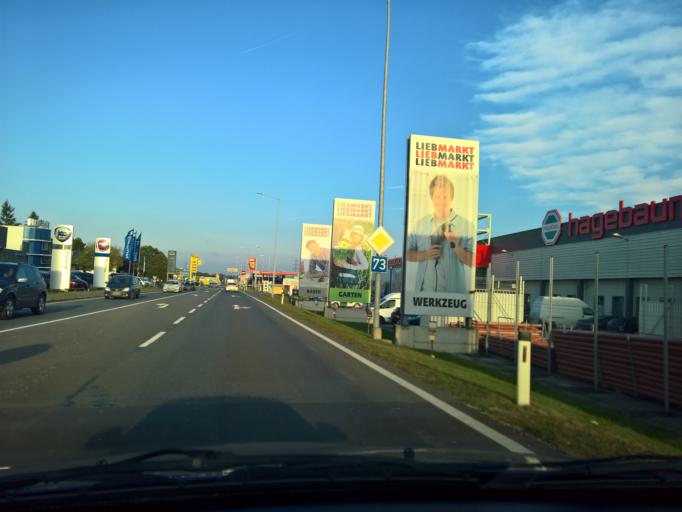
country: AT
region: Styria
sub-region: Politischer Bezirk Leibnitz
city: Kaindorf an der Sulm
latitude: 46.8039
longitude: 15.5566
